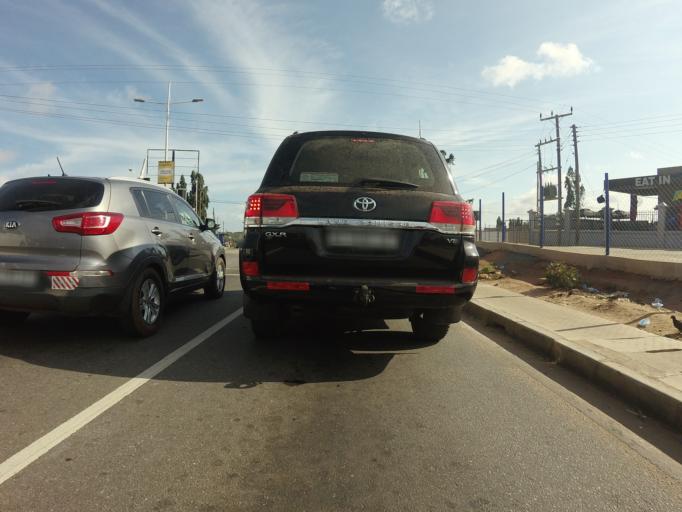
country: GH
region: Greater Accra
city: Medina Estates
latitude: 5.6249
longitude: -0.1529
